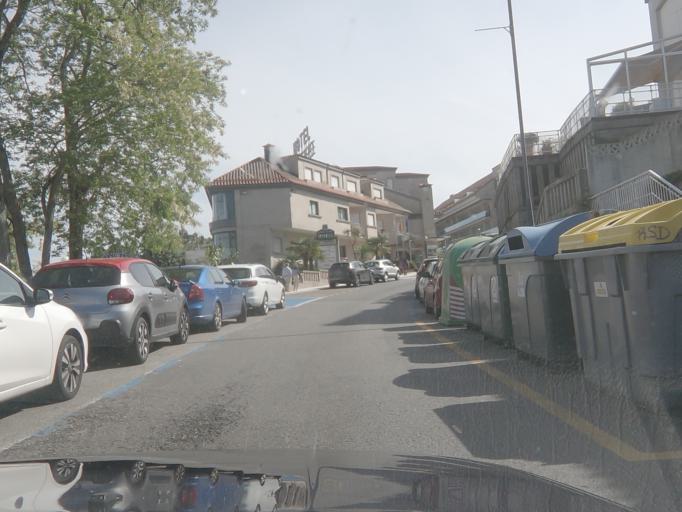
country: ES
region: Galicia
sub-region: Provincia de Pontevedra
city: Sanxenxo
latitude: 42.4001
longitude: -8.8167
